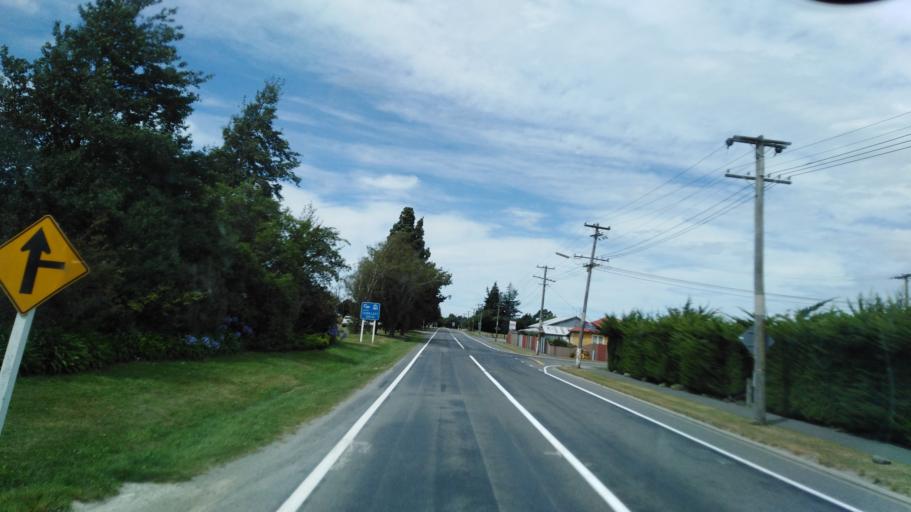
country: NZ
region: Canterbury
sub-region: Selwyn District
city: Darfield
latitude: -43.3897
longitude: 172.0209
